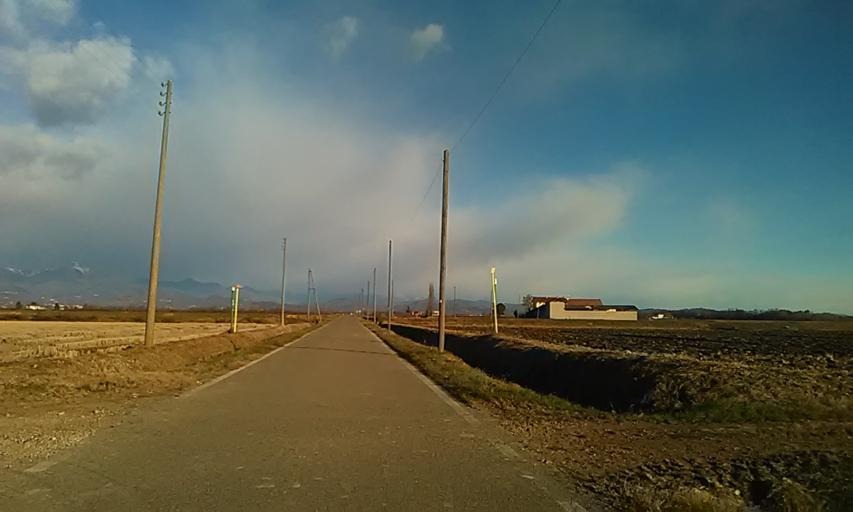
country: IT
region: Piedmont
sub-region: Provincia di Vercelli
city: Buronzo
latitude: 45.5084
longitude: 8.2701
